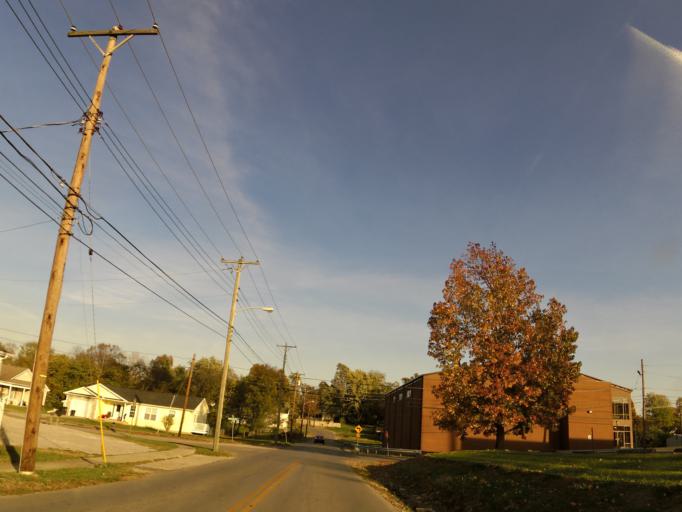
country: US
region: Kentucky
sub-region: Garrard County
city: Lancaster
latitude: 37.6206
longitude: -84.5774
